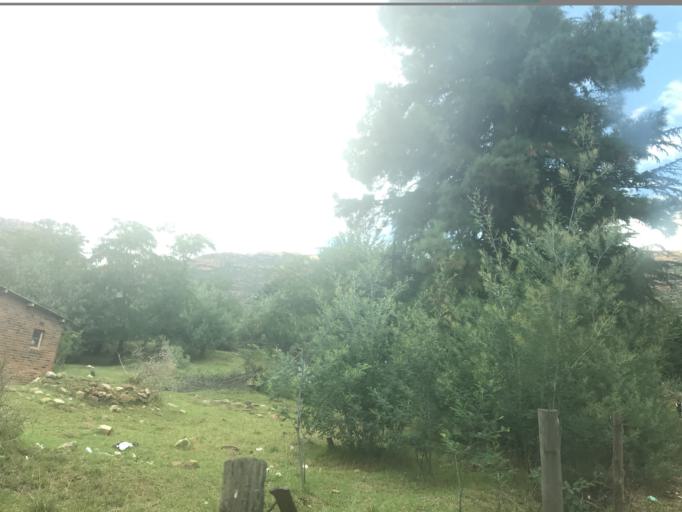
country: LS
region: Maseru
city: Nako
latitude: -29.6302
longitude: 27.5034
